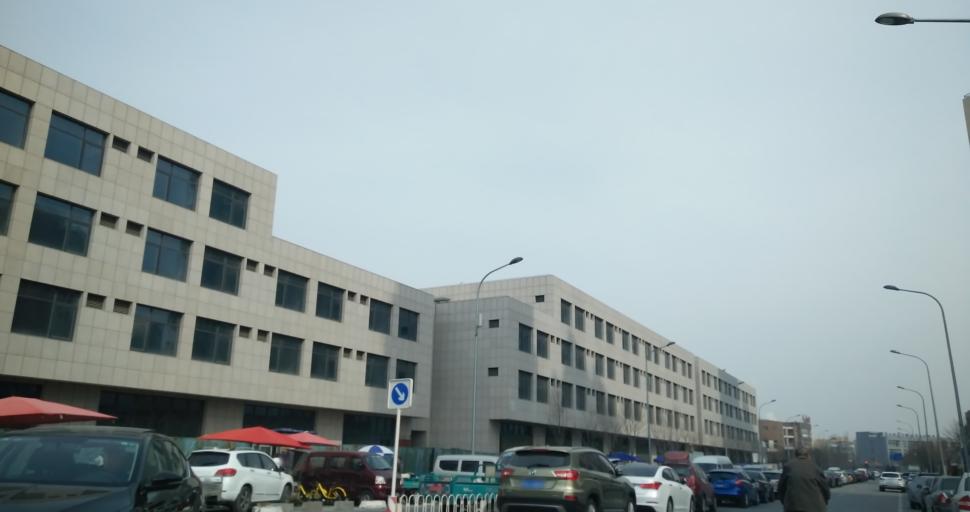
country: CN
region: Beijing
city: Jiugong
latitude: 39.8541
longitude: 116.4962
